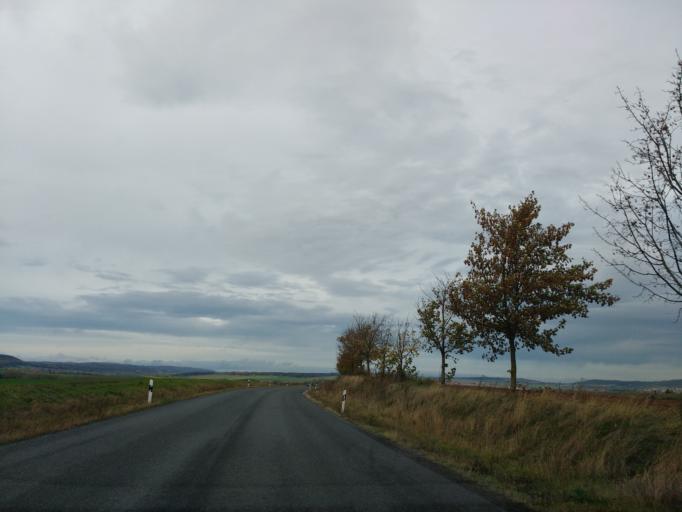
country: DE
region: Thuringia
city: Deuna
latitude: 51.3562
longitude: 10.4656
